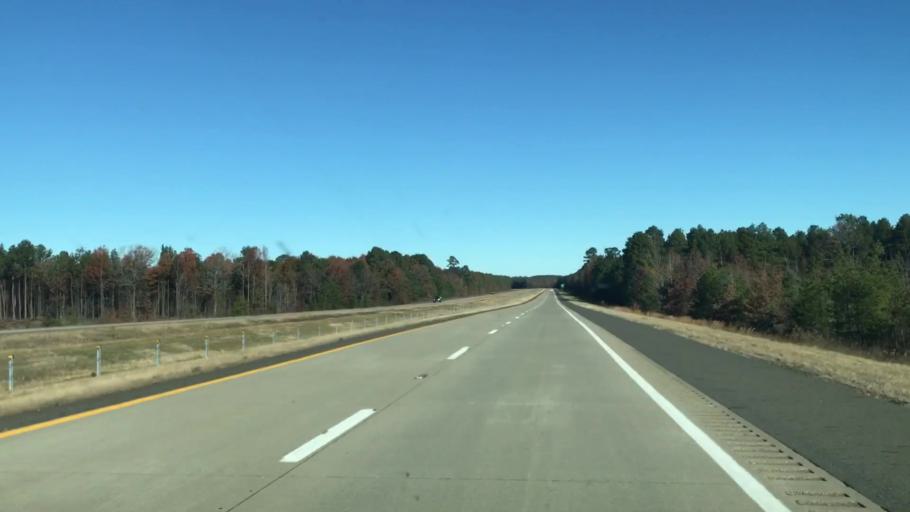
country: US
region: Texas
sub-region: Bowie County
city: Texarkana
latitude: 33.2265
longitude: -93.8732
